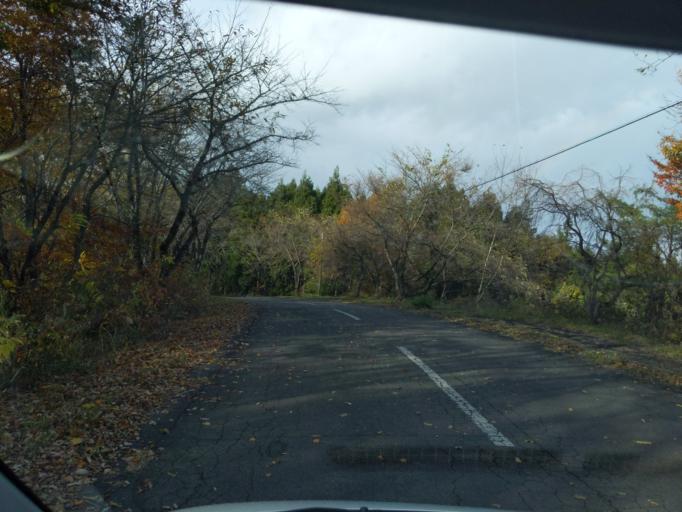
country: JP
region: Iwate
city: Mizusawa
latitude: 39.0281
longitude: 141.0930
